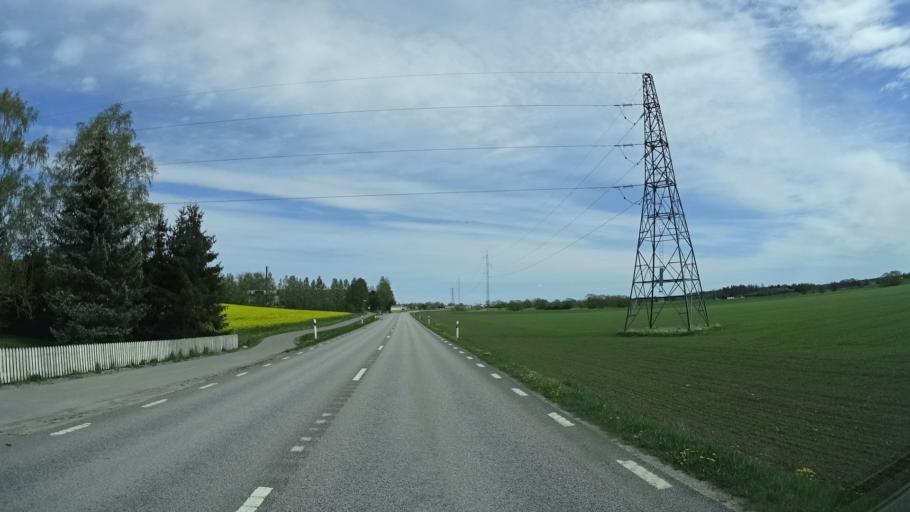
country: SE
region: OEstergoetland
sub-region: Linkopings Kommun
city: Vikingstad
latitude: 58.3736
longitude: 15.4058
